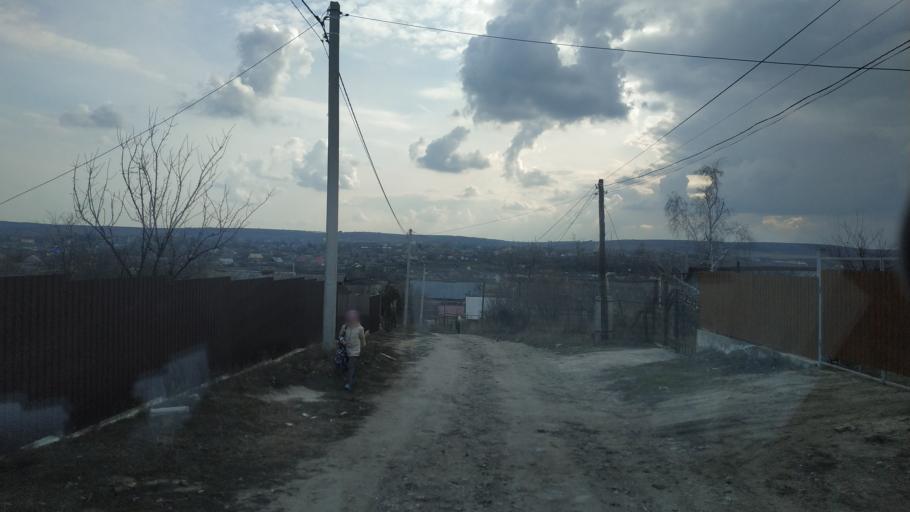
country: MD
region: Anenii Noi
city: Anenii Noi
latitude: 46.8935
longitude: 29.2982
